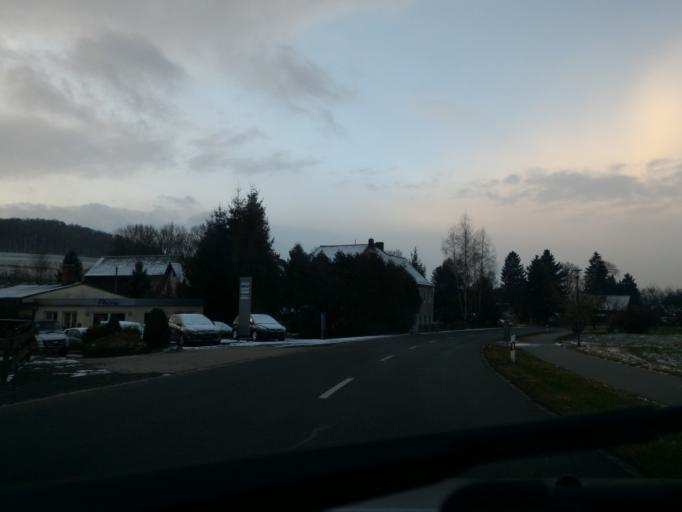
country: DE
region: Saxony
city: Leutersdorf
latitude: 50.9444
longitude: 14.6296
